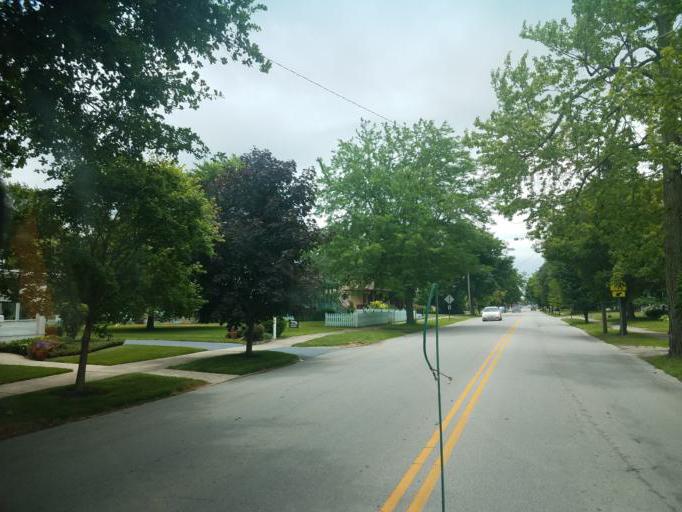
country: US
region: Ohio
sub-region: Hardin County
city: Ada
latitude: 40.7755
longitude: -83.8233
